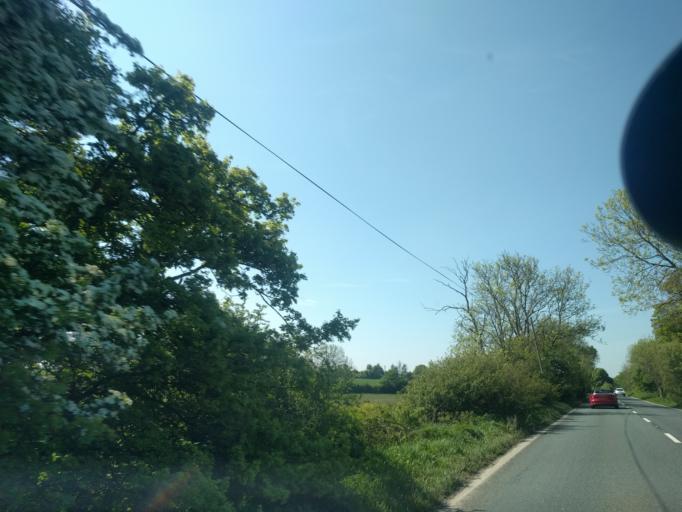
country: GB
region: England
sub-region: Somerset
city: Ilchester
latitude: 51.0318
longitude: -2.6607
